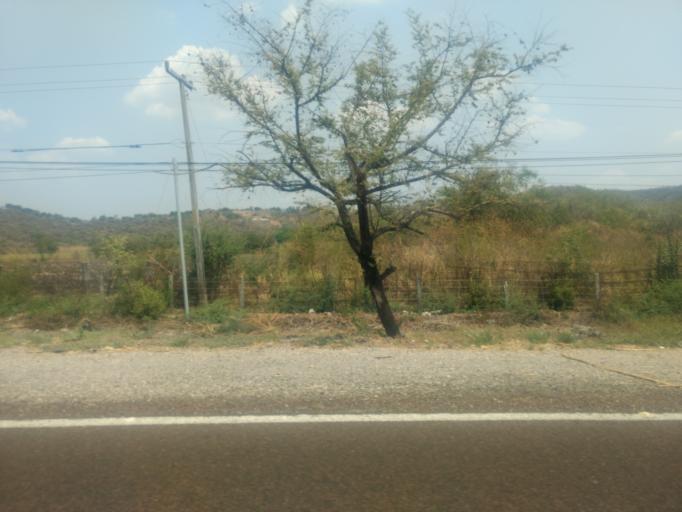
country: MX
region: Morelos
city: Puente de Ixtla
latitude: 18.6374
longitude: -99.3130
